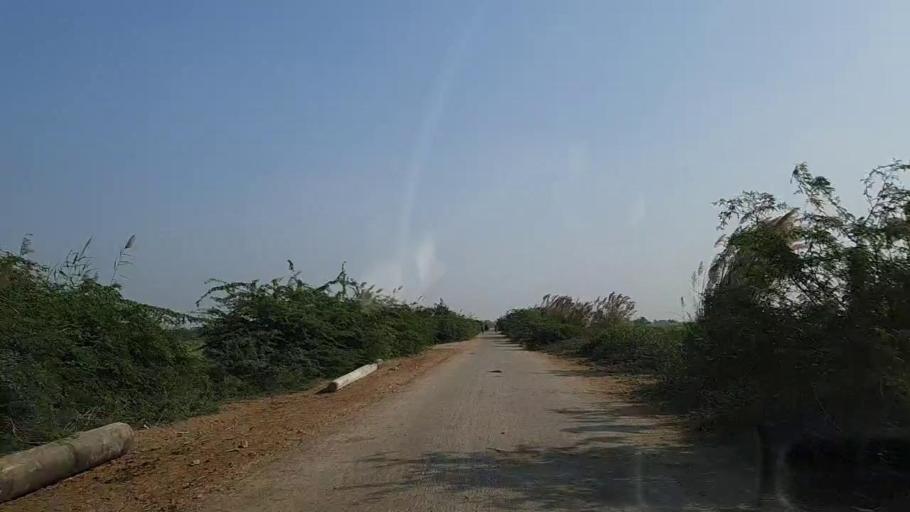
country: PK
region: Sindh
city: Mirpur Sakro
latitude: 24.6259
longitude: 67.6543
